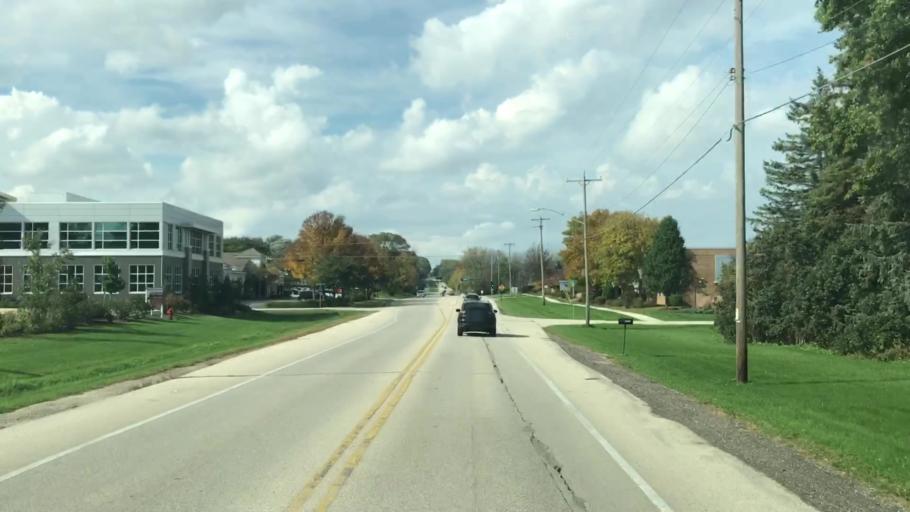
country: US
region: Wisconsin
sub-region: Waukesha County
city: Elm Grove
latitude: 43.0604
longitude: -88.0828
